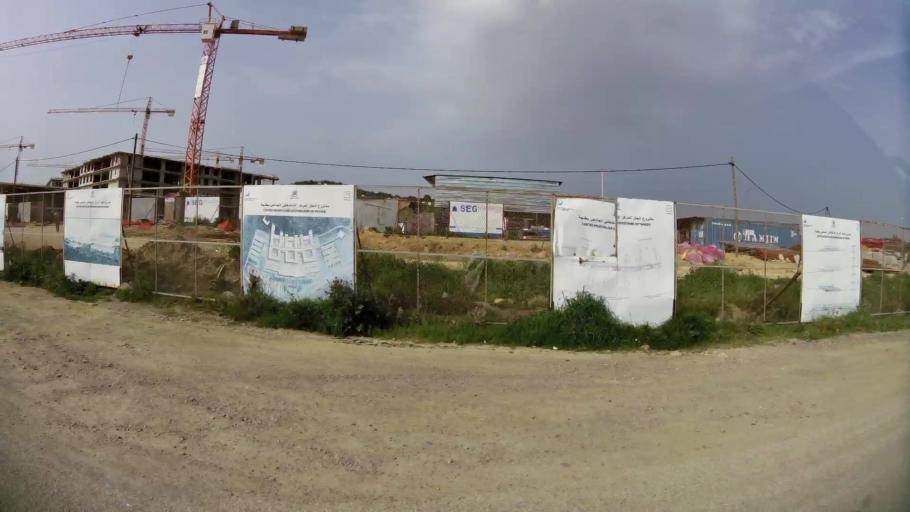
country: MA
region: Tanger-Tetouan
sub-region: Tanger-Assilah
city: Boukhalef
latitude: 35.6823
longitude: -5.9264
